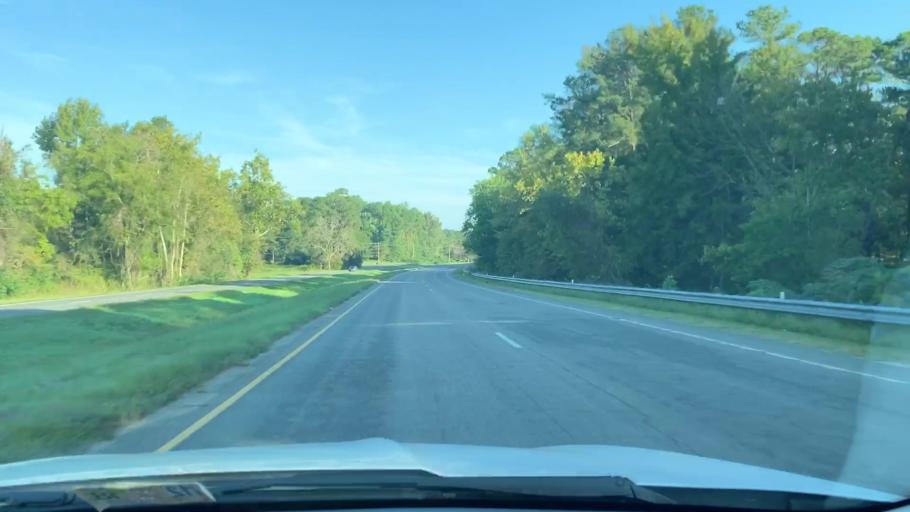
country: US
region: Virginia
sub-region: Lancaster County
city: Kilmarnock
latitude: 37.6809
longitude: -76.3767
